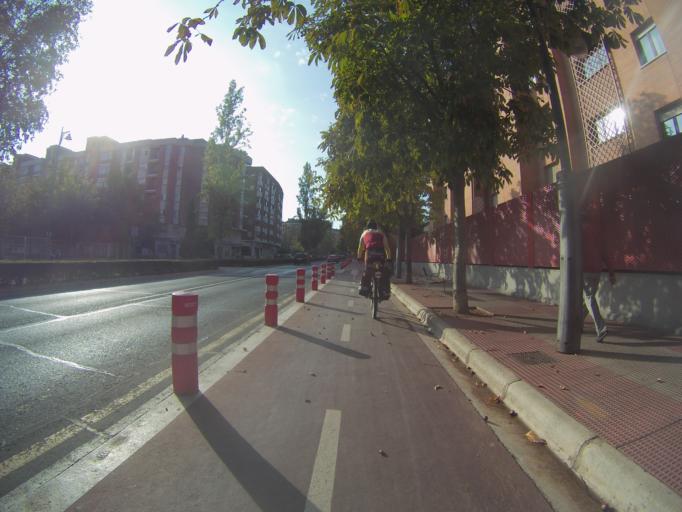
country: ES
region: La Rioja
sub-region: Provincia de La Rioja
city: Logrono
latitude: 42.4624
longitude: -2.4618
